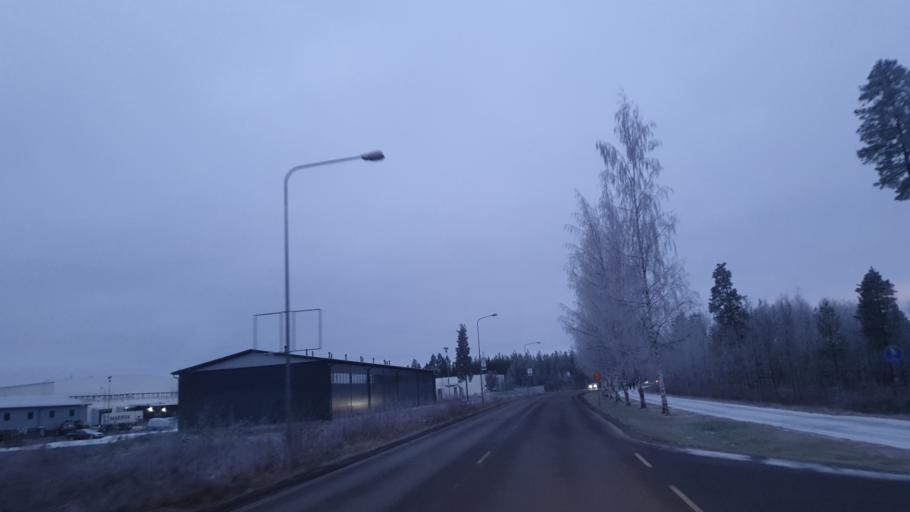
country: FI
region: Southern Ostrobothnia
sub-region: Seinaejoki
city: Nurmo
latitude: 62.7802
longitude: 22.8972
